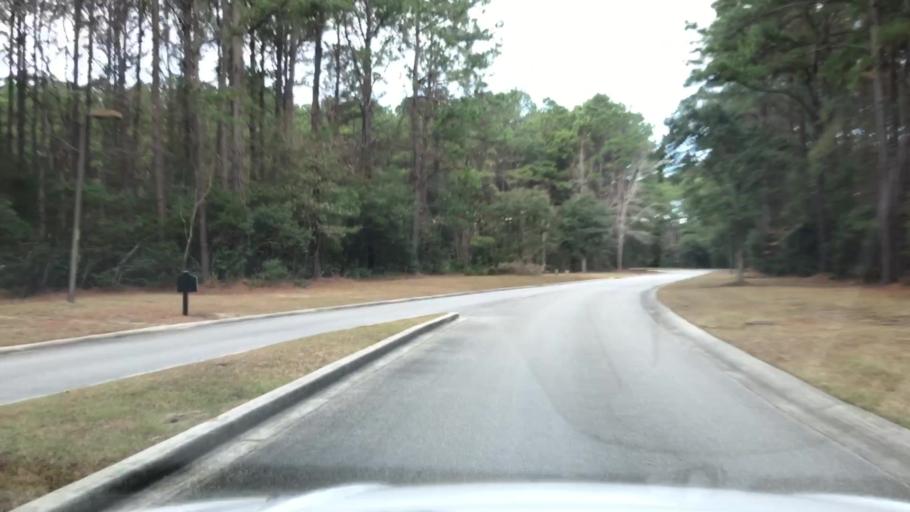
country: US
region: South Carolina
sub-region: Charleston County
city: Isle of Palms
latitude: 32.9073
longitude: -79.7215
